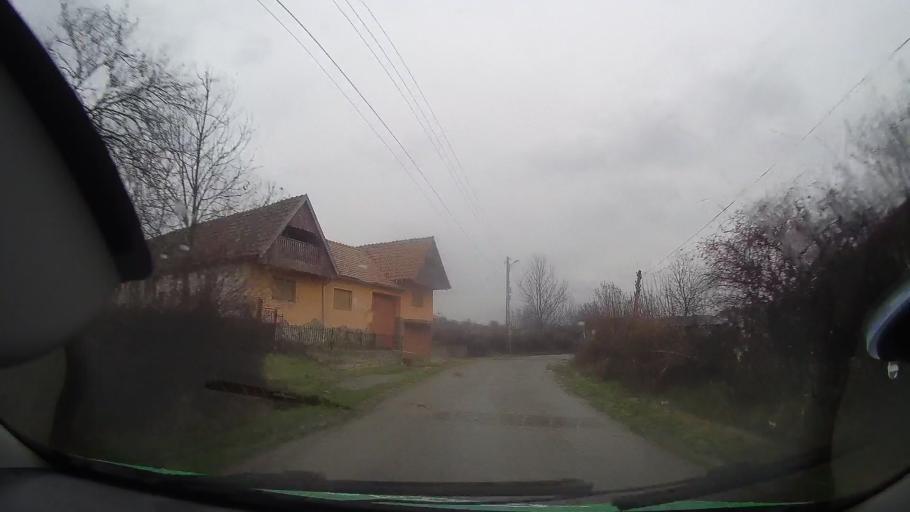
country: RO
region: Bihor
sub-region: Comuna Uileacu de Beius
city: Uileacu de Beius
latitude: 46.7063
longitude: 22.2233
